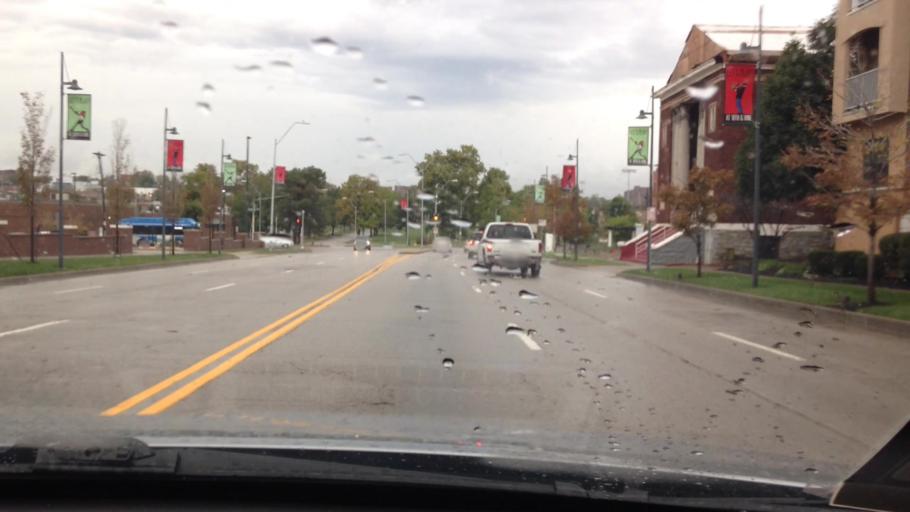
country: US
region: Missouri
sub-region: Jackson County
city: Kansas City
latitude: 39.0901
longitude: -94.5645
